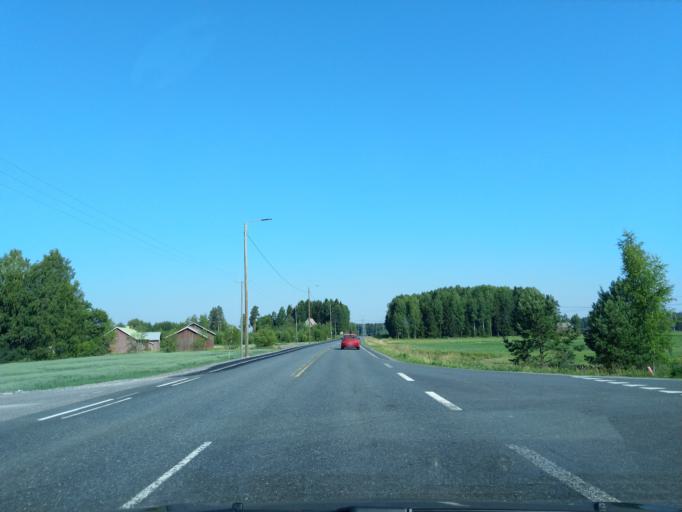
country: FI
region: Haeme
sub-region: Forssa
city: Forssa
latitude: 60.7683
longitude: 23.6824
